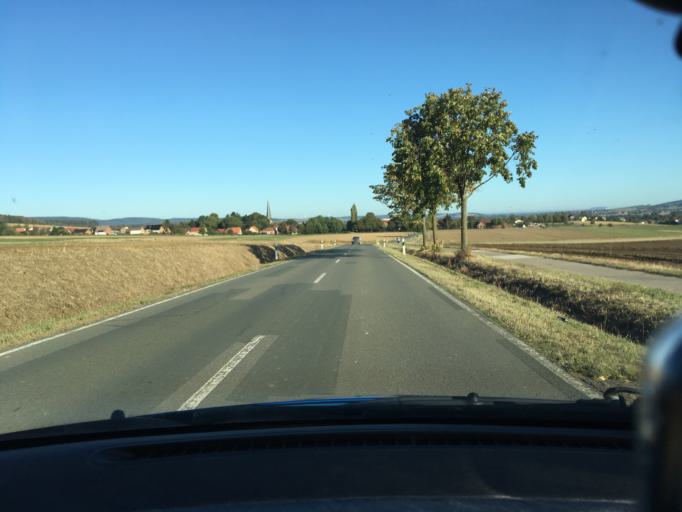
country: DE
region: Lower Saxony
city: Hulsede
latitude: 52.2177
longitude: 9.3872
